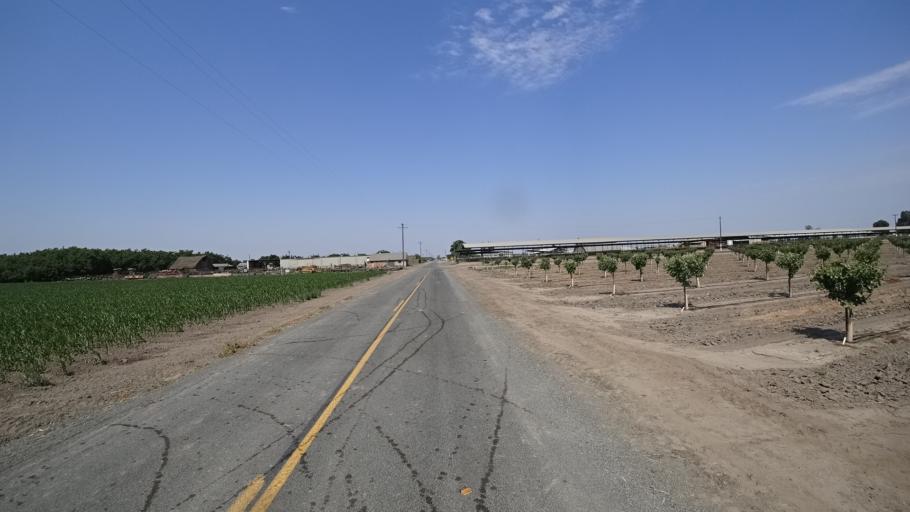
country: US
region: California
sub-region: Fresno County
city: Riverdale
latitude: 36.3948
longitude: -119.7793
